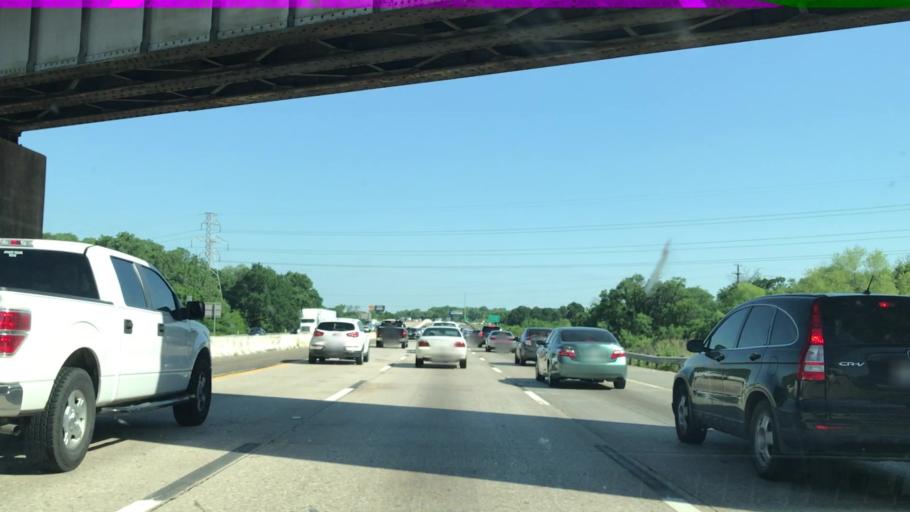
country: US
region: Texas
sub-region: Tarrant County
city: Euless
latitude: 32.8172
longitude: -97.0590
